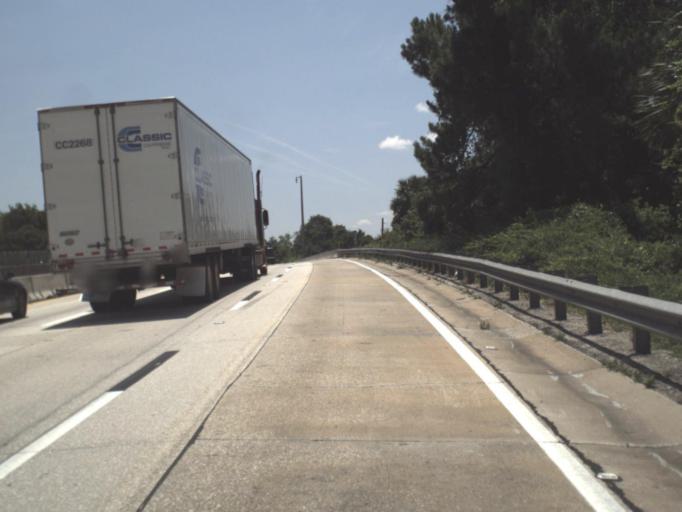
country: US
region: Florida
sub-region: Duval County
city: Jacksonville
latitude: 30.3008
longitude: -81.6404
